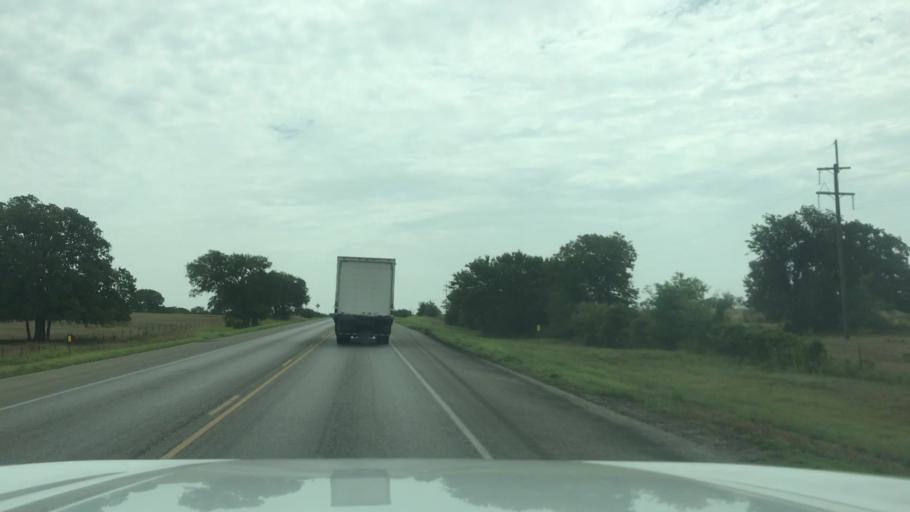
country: US
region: Texas
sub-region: Comanche County
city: De Leon
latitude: 32.0924
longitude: -98.4461
